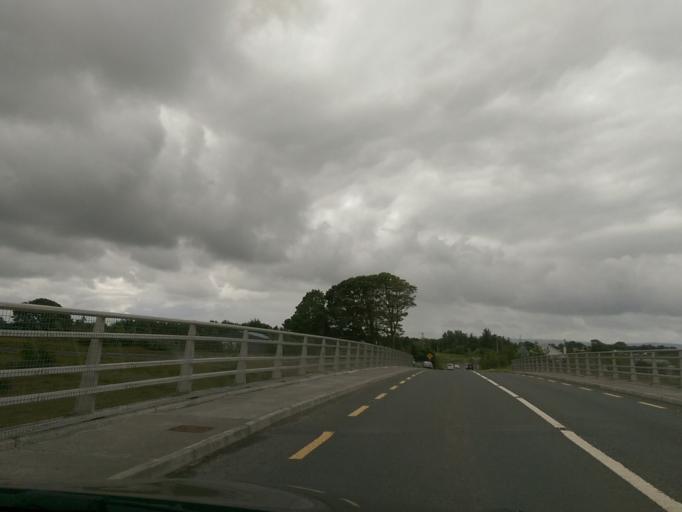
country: IE
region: Connaught
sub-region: County Galway
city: Loughrea
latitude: 53.2785
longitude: -8.5299
